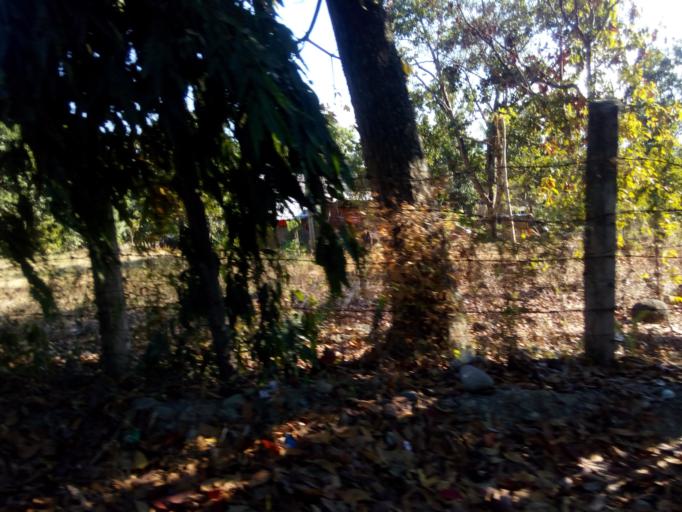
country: PH
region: Central Visayas
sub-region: Province of Negros Oriental
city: Valencia
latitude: 9.3134
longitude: 123.2597
